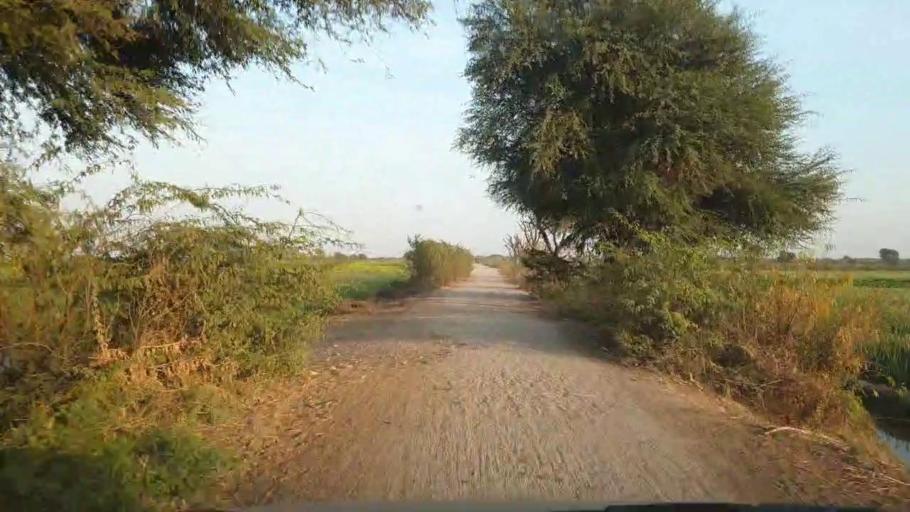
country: PK
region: Sindh
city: Chambar
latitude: 25.2837
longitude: 68.8259
